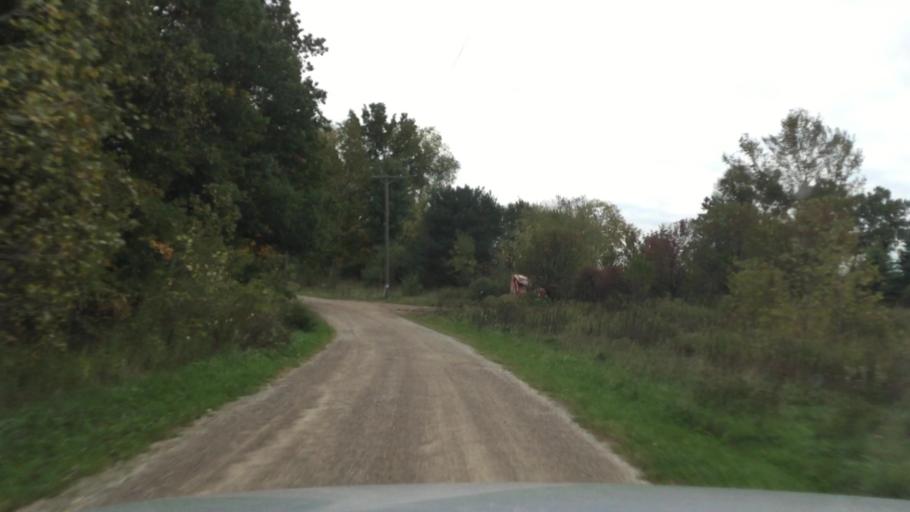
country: US
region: Michigan
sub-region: Genesee County
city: Fenton
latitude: 42.6801
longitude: -83.7393
